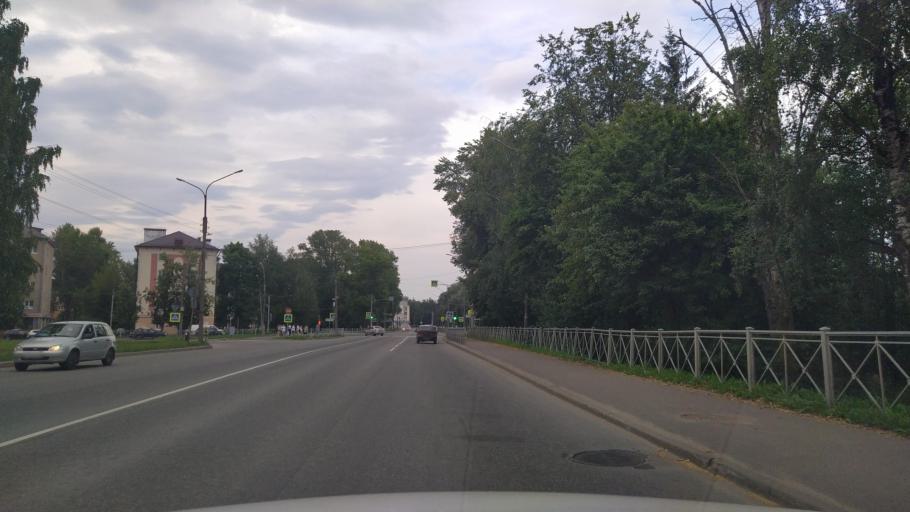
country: RU
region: Novgorod
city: Velikiy Novgorod
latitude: 58.5212
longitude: 31.2549
